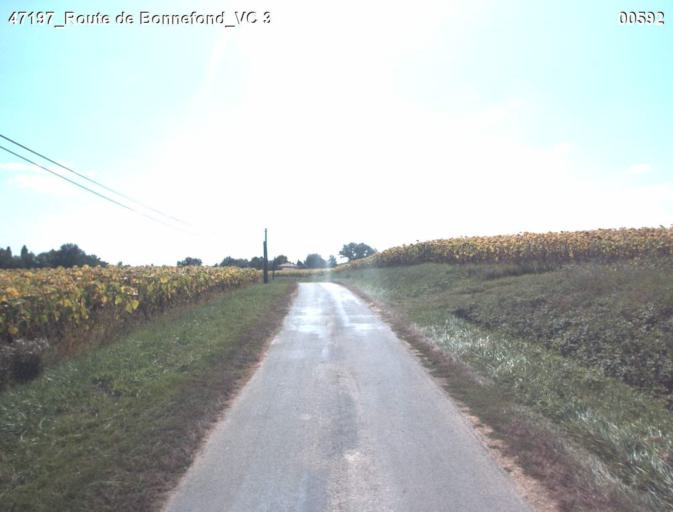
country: FR
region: Aquitaine
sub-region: Departement du Lot-et-Garonne
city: Laplume
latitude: 44.1006
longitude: 0.4754
